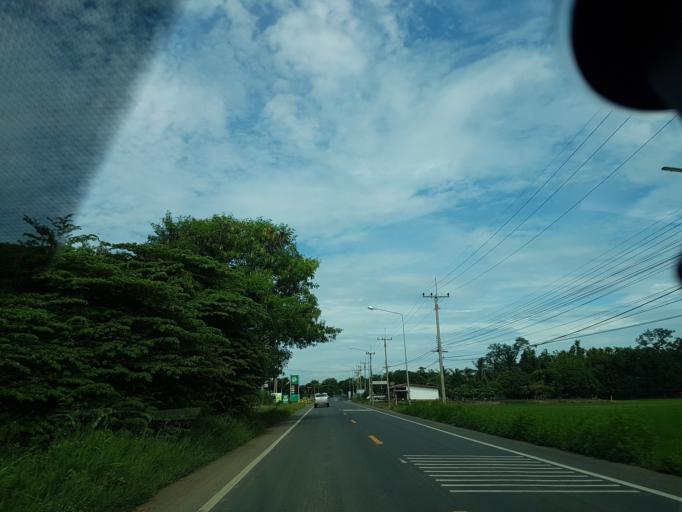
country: TH
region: Ang Thong
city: Chaiyo
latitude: 14.7323
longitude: 100.5136
